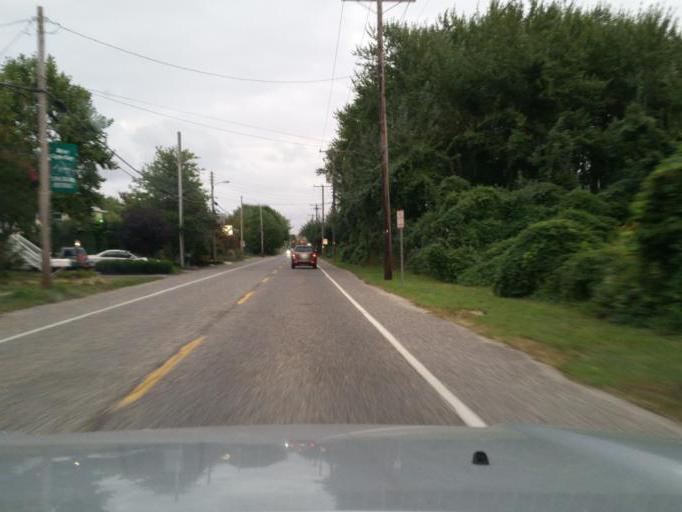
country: US
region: New Jersey
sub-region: Cape May County
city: West Cape May
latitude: 38.9365
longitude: -74.9367
